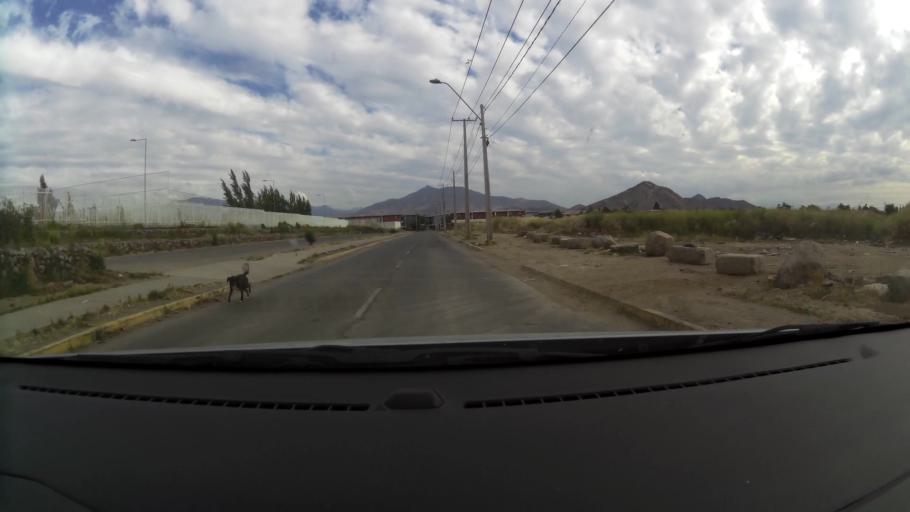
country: CL
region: Santiago Metropolitan
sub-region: Provincia de Cordillera
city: Puente Alto
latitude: -33.6243
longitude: -70.6178
